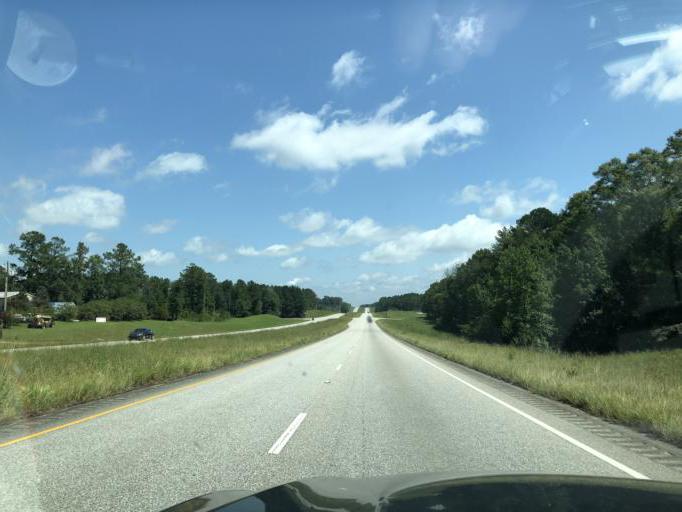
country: US
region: Alabama
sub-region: Barbour County
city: Eufaula
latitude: 31.7490
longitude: -85.2298
